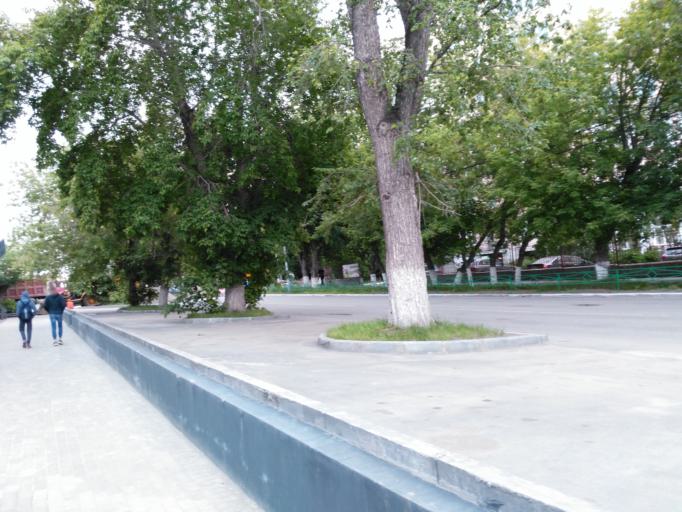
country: RU
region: Chelyabinsk
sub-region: Gorod Chelyabinsk
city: Chelyabinsk
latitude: 55.1632
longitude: 61.4127
